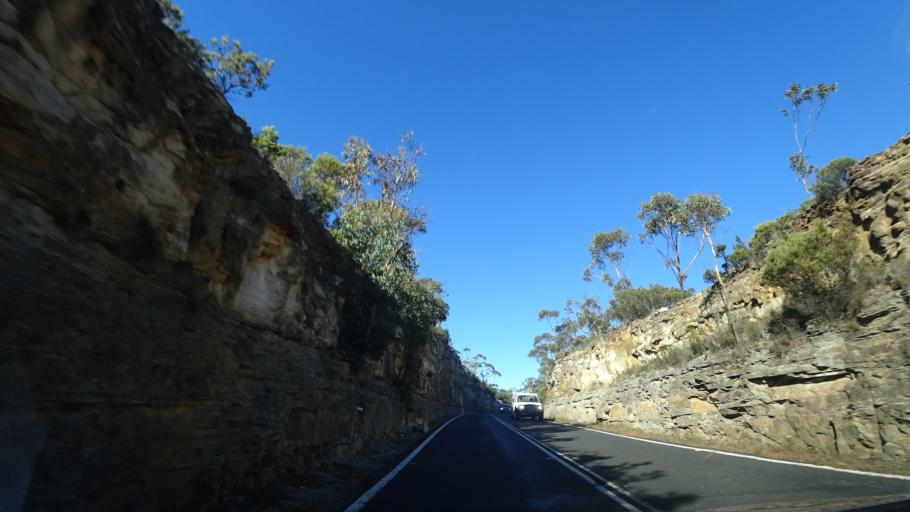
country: AU
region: New South Wales
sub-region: Blue Mountains Municipality
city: Blackheath
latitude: -33.5540
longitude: 150.3793
